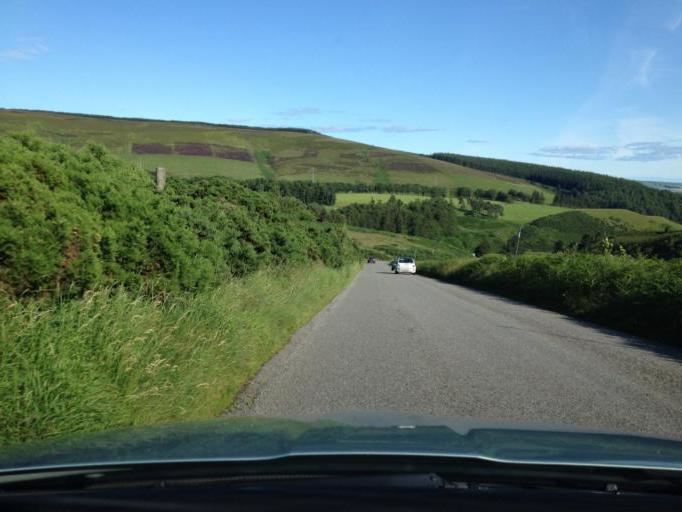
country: GB
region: Scotland
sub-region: Aberdeenshire
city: Laurencekirk
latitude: 56.8979
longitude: -2.5578
